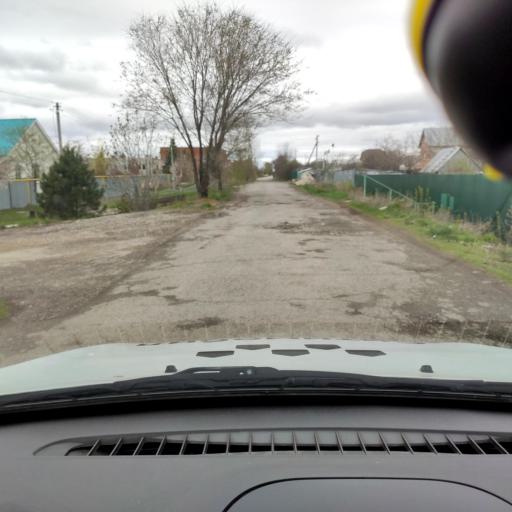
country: RU
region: Samara
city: Tol'yatti
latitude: 53.5763
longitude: 49.3288
